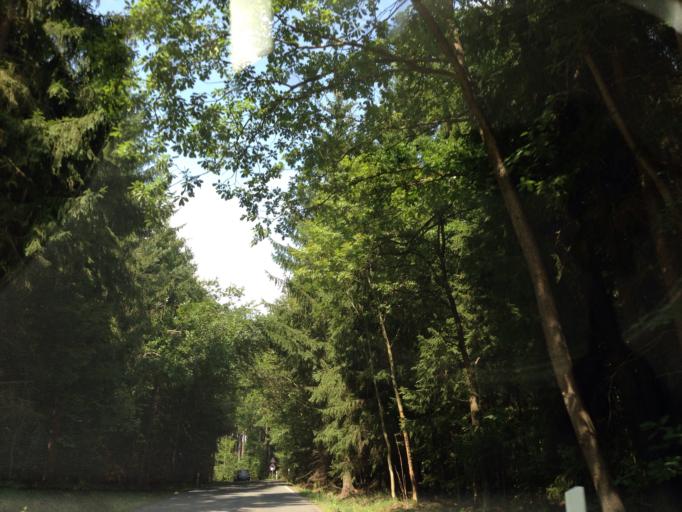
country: DE
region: Thuringia
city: Herschdorf
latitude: 50.7233
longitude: 11.5237
